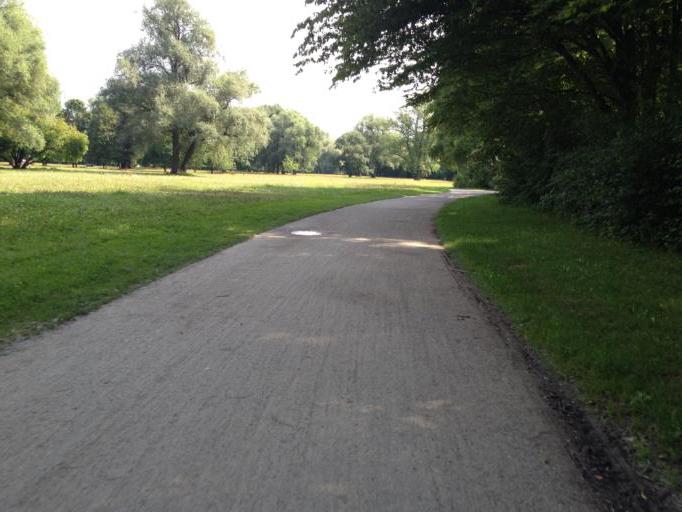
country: DE
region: Bavaria
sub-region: Upper Bavaria
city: Bogenhausen
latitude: 48.1600
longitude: 11.6054
